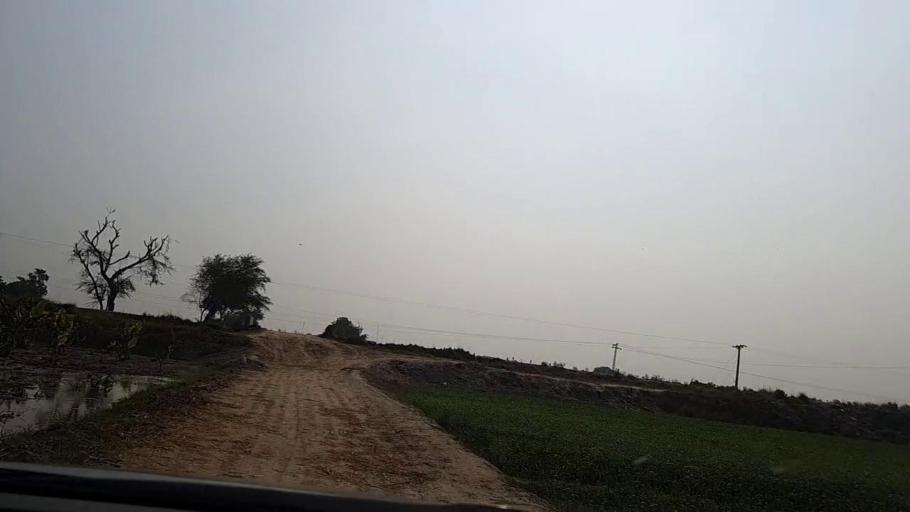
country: PK
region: Sindh
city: Sakrand
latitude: 26.1399
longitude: 68.2340
